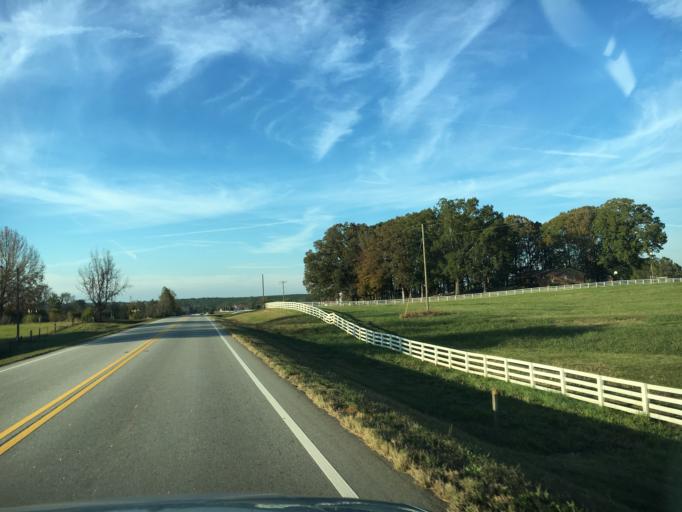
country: US
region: Georgia
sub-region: Wilkes County
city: Washington
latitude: 33.9207
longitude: -82.7527
